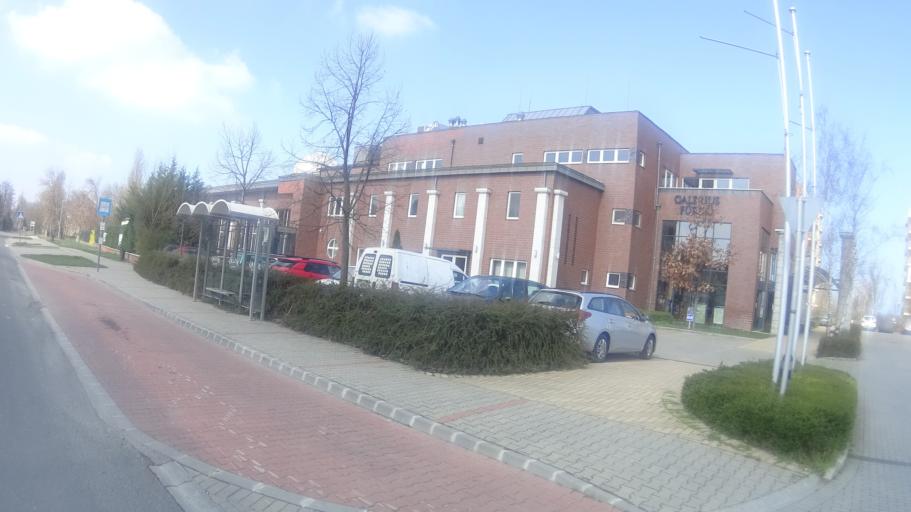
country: HU
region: Somogy
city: Siofok
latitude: 46.9260
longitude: 18.1001
